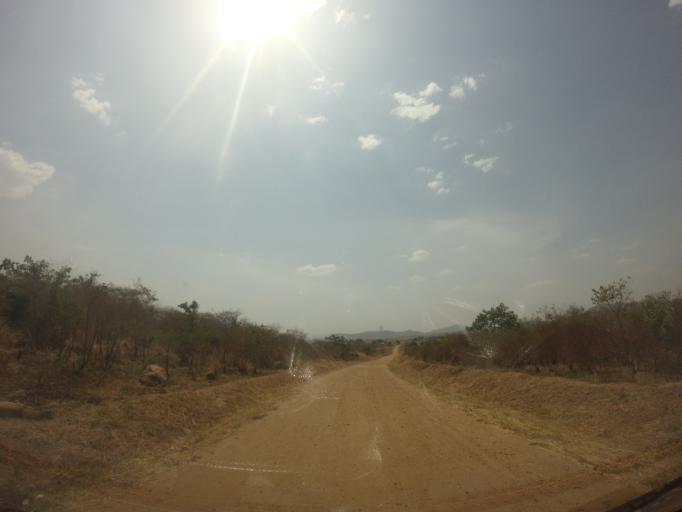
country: UG
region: Northern Region
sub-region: Arua District
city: Arua
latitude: 2.9088
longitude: 31.0608
